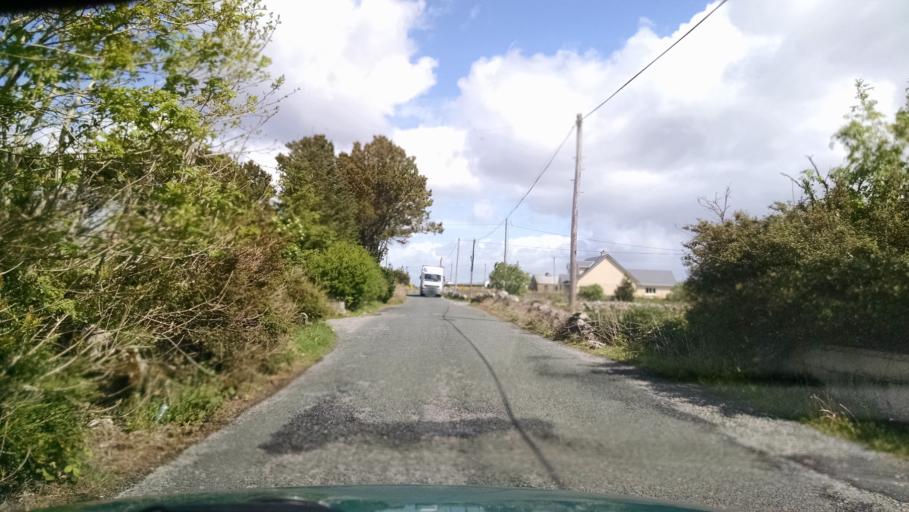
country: IE
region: Connaught
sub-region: County Galway
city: Oughterard
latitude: 53.2785
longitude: -9.5968
